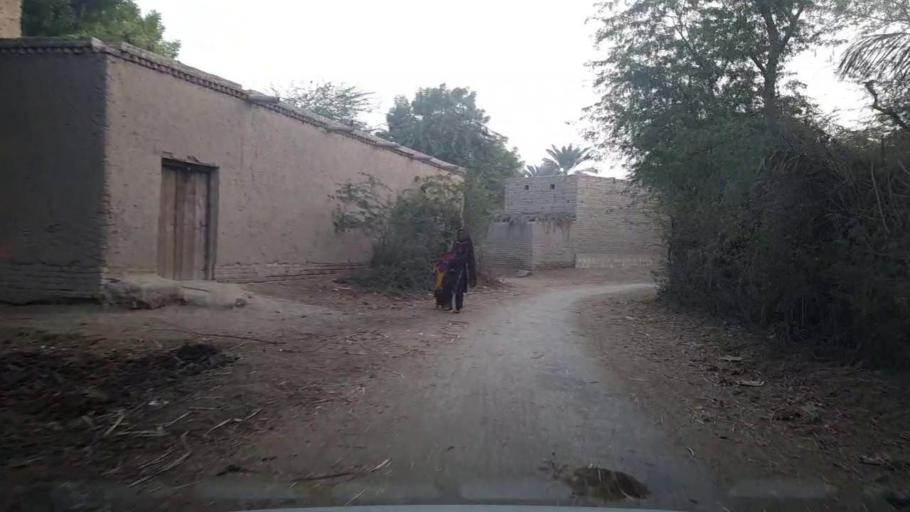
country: PK
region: Sindh
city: Kot Diji
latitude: 27.3346
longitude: 68.6399
